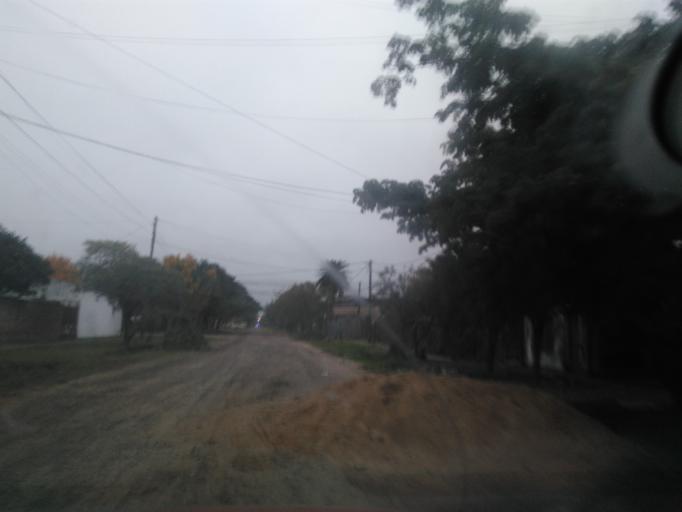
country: AR
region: Chaco
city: Resistencia
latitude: -27.4715
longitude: -58.9933
